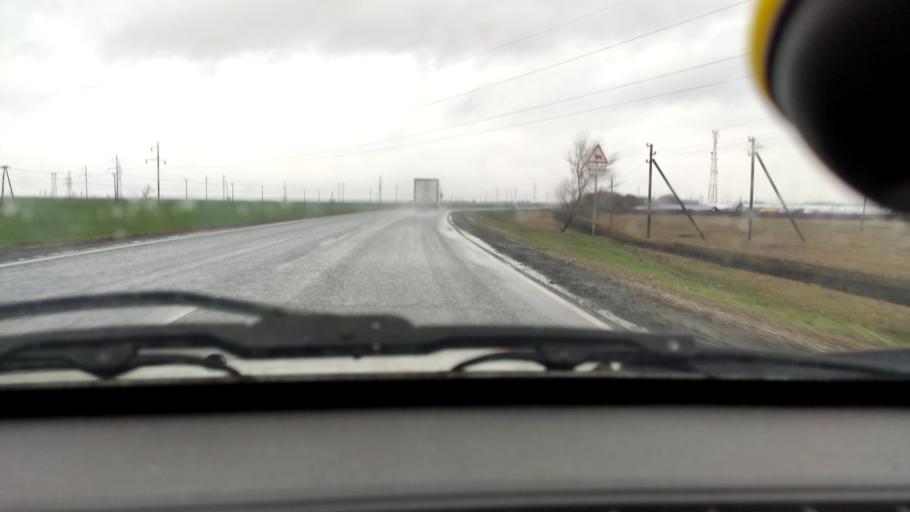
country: RU
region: Samara
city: Povolzhskiy
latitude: 53.6357
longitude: 49.6585
